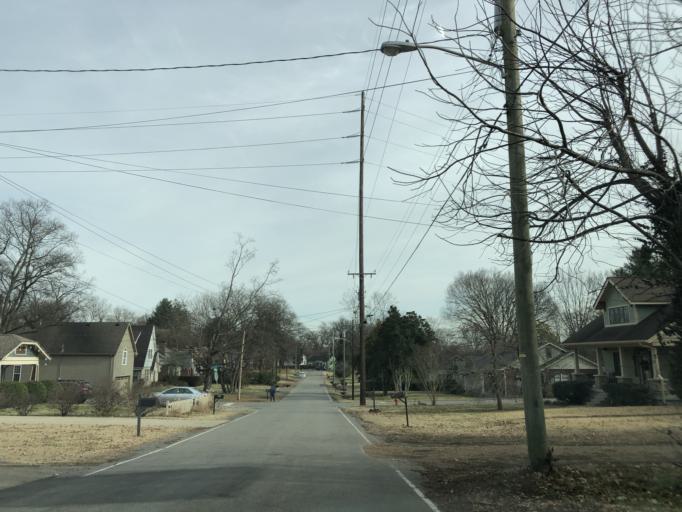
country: US
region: Tennessee
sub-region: Davidson County
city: Nashville
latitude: 36.2113
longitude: -86.7260
